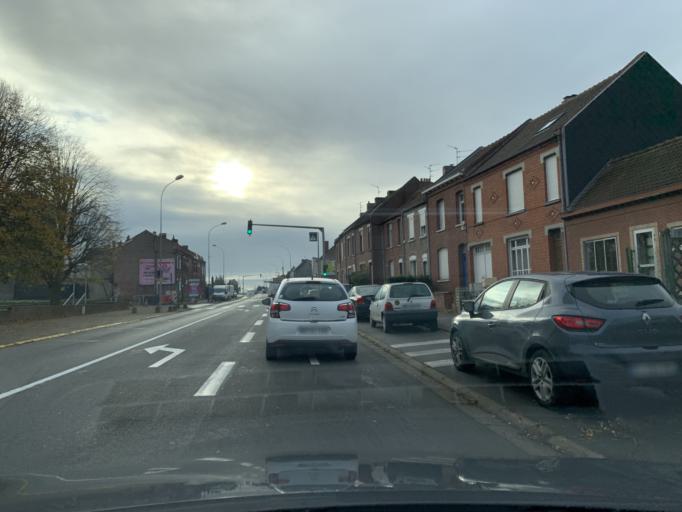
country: FR
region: Nord-Pas-de-Calais
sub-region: Departement du Nord
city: Lambres-lez-Douai
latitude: 50.3506
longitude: 3.0870
